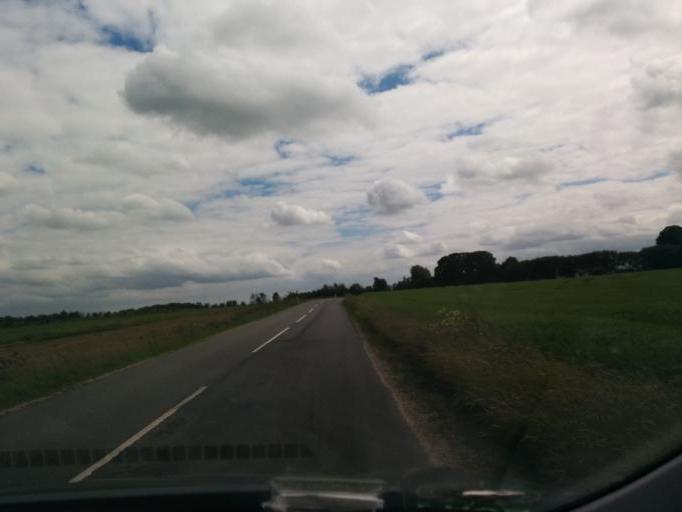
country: DK
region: Central Jutland
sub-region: Syddjurs Kommune
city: Ryomgard
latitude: 56.4038
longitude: 10.5617
